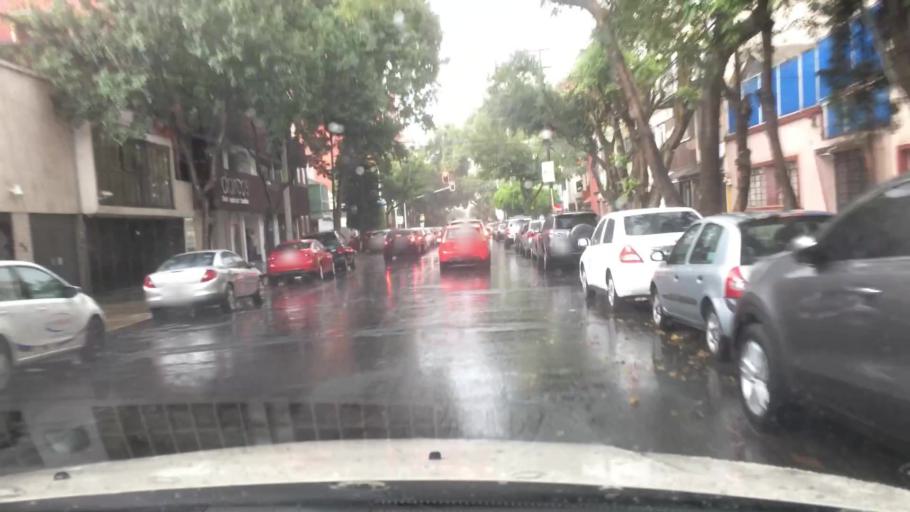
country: MX
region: Mexico City
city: Colonia del Valle
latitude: 19.3695
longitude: -99.1749
